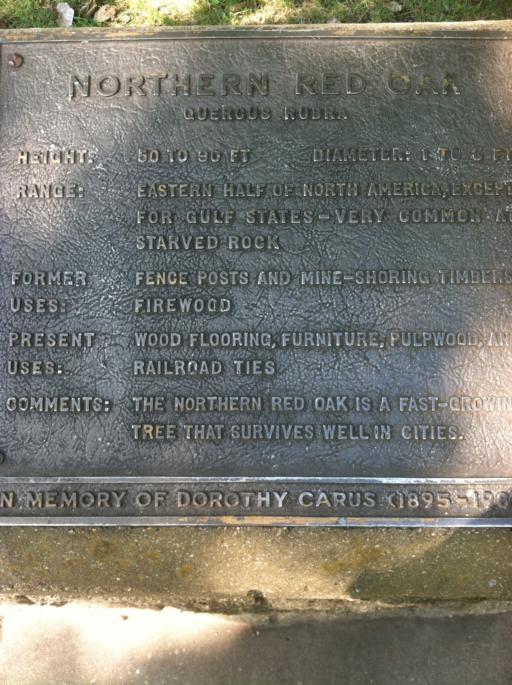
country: US
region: Illinois
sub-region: LaSalle County
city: Deer Park
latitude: 41.3211
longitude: -88.9932
